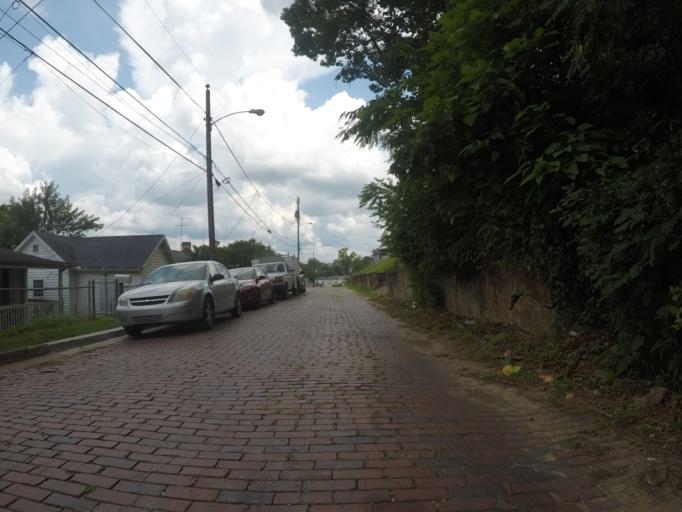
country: US
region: West Virginia
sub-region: Cabell County
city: Huntington
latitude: 38.4237
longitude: -82.3848
